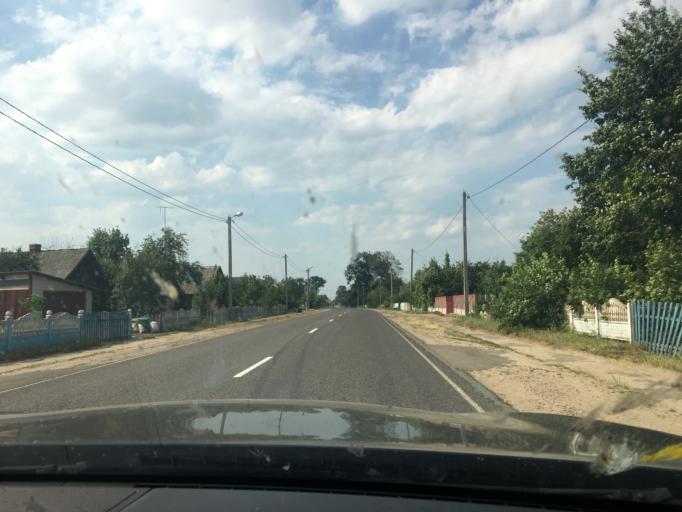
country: BY
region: Brest
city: Pruzhany
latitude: 52.6267
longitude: 24.3227
